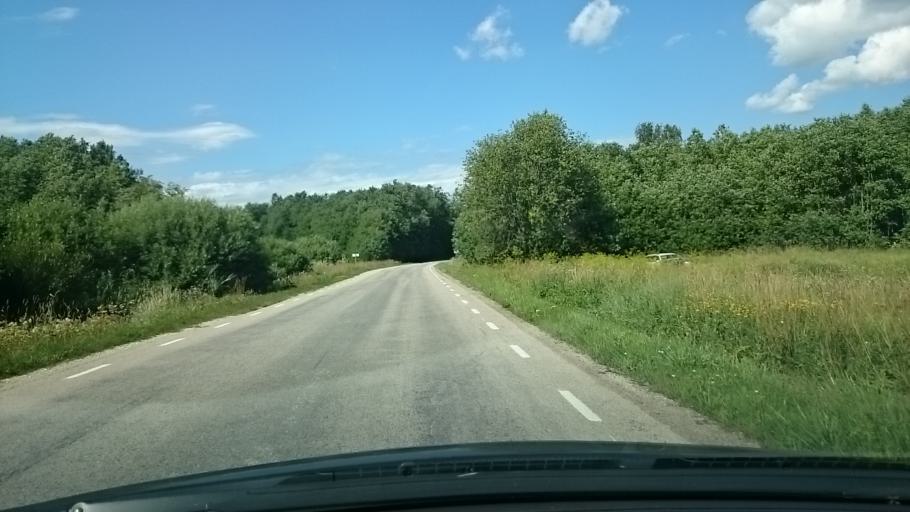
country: EE
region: Laeaene
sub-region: Haapsalu linn
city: Haapsalu
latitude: 59.0424
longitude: 23.5084
